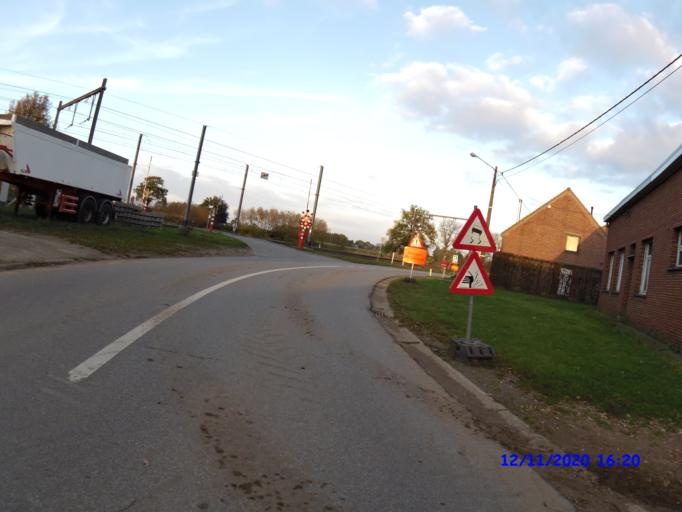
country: BE
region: Flanders
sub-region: Provincie Antwerpen
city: Meerhout
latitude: 51.1812
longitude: 5.0627
